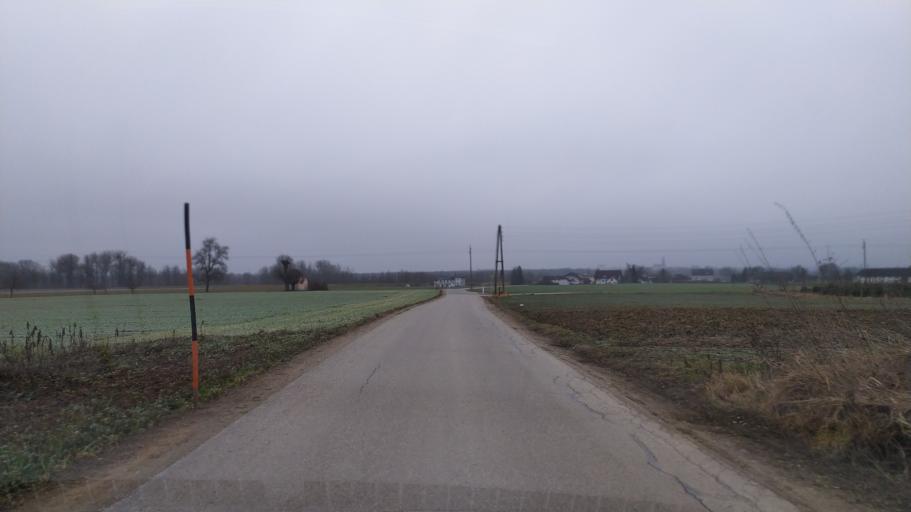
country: AT
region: Upper Austria
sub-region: Politischer Bezirk Perg
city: Perg
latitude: 48.1952
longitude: 14.7201
